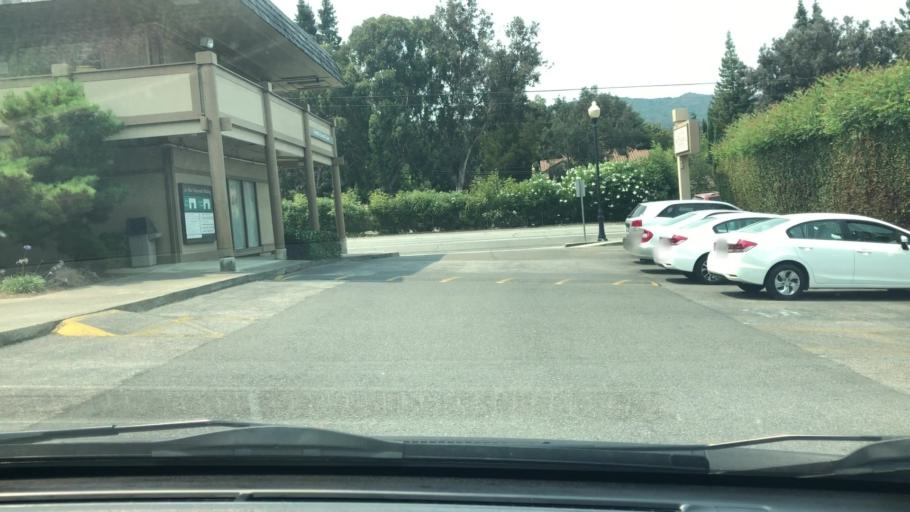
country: US
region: California
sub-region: Santa Clara County
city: Loyola
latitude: 37.3554
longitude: -122.0901
